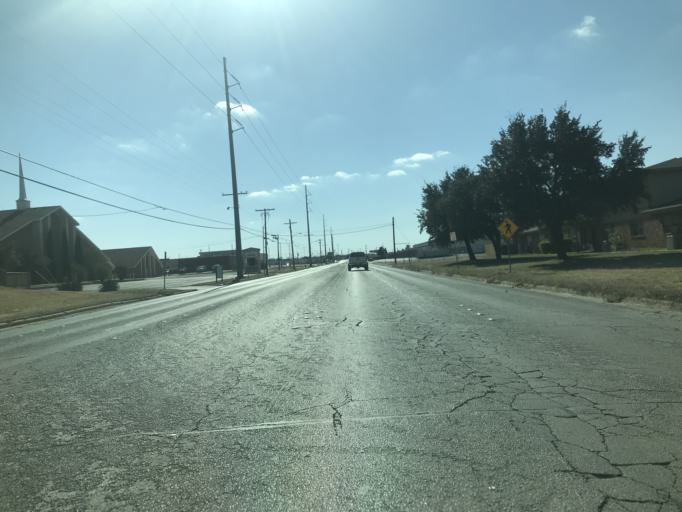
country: US
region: Texas
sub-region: Taylor County
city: Abilene
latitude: 32.4579
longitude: -99.7787
